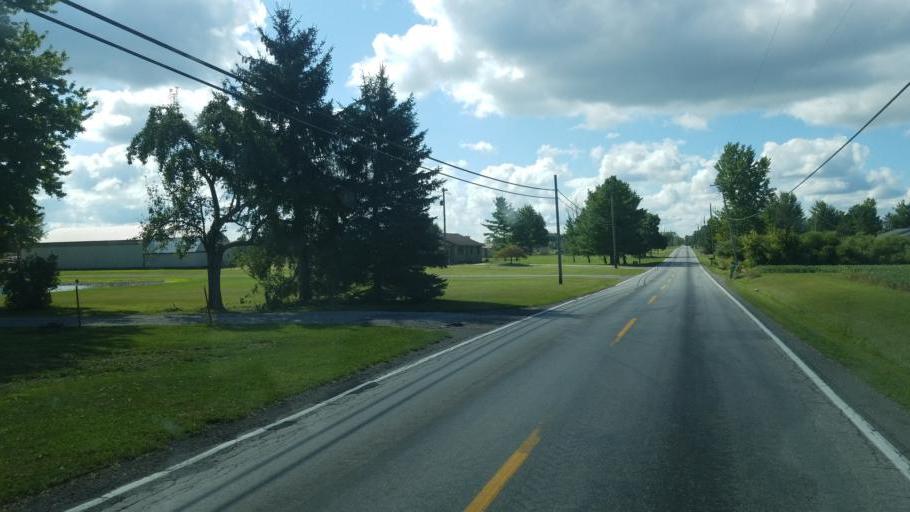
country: US
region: Ohio
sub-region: Lorain County
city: Lagrange
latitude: 41.2333
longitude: -82.1392
